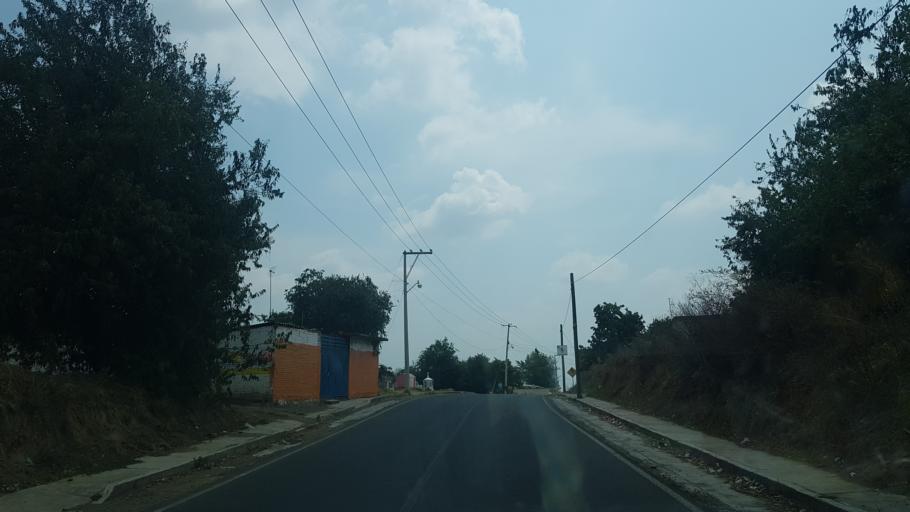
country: MX
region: Puebla
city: Domingo Arenas
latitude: 19.1411
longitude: -98.4675
